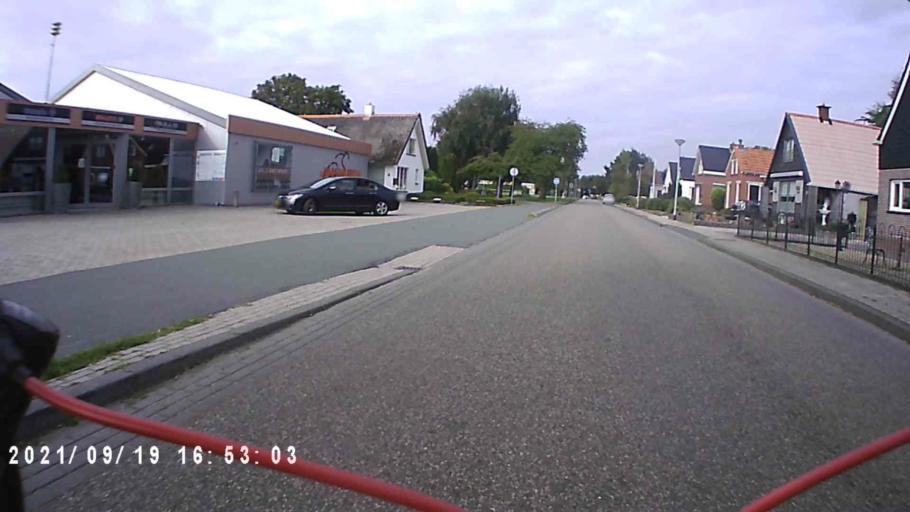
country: NL
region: Groningen
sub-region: Gemeente  Oldambt
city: Winschoten
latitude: 53.1824
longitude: 7.0783
